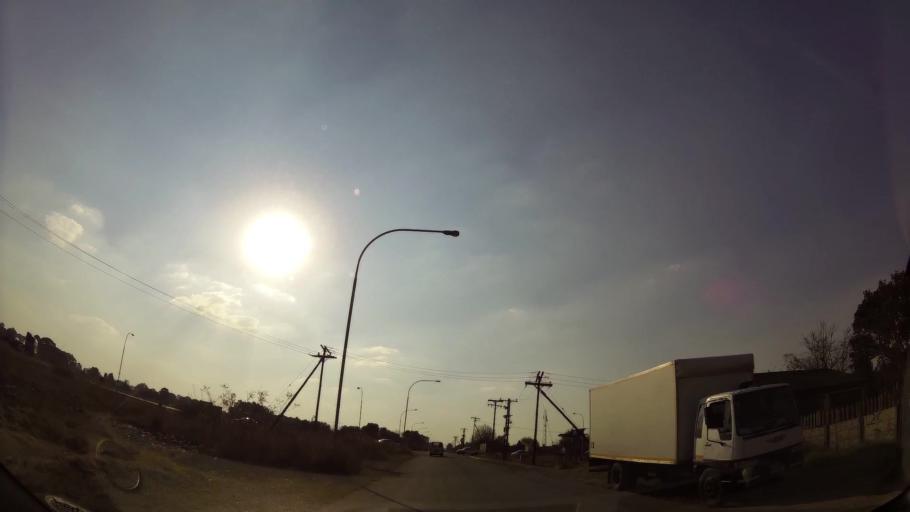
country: ZA
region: Gauteng
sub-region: Ekurhuleni Metropolitan Municipality
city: Benoni
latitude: -26.1254
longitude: 28.3936
